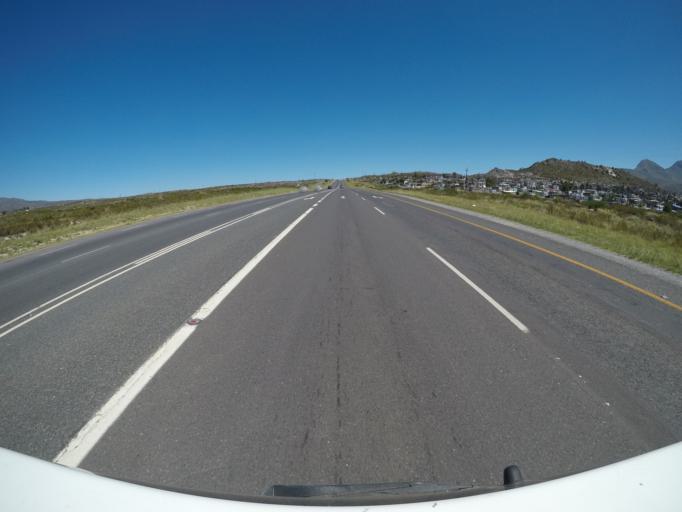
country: ZA
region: Western Cape
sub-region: Overberg District Municipality
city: Grabouw
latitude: -34.1621
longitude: 18.9842
